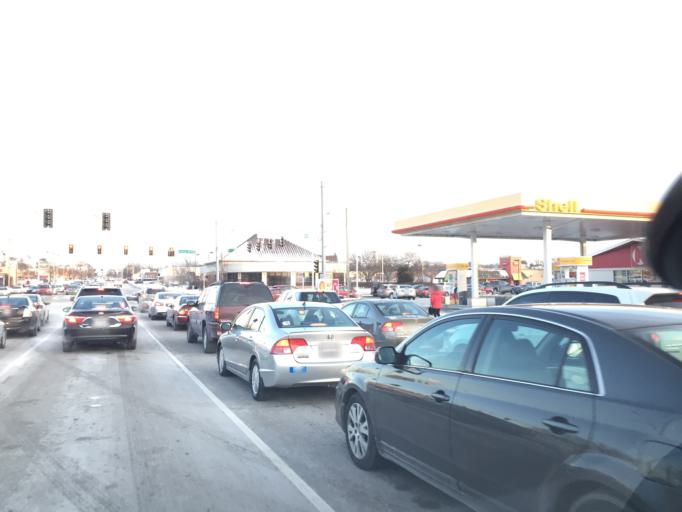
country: US
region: Indiana
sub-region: Monroe County
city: Bloomington
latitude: 39.1642
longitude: -86.4990
